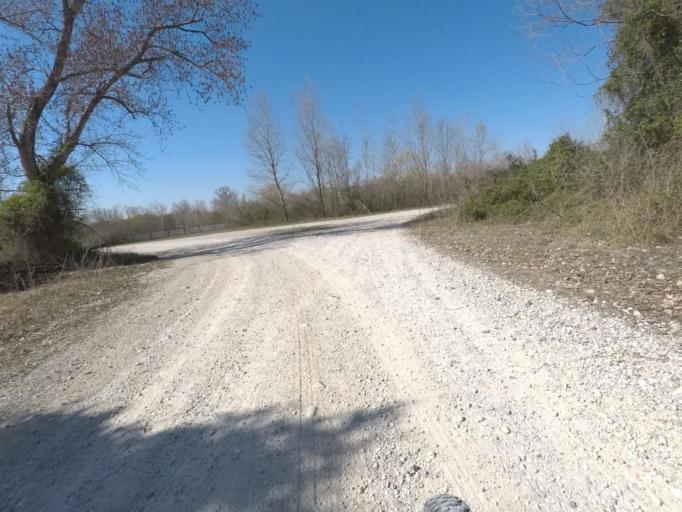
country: IT
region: Friuli Venezia Giulia
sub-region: Provincia di Udine
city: Remanzacco
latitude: 46.0697
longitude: 13.2965
